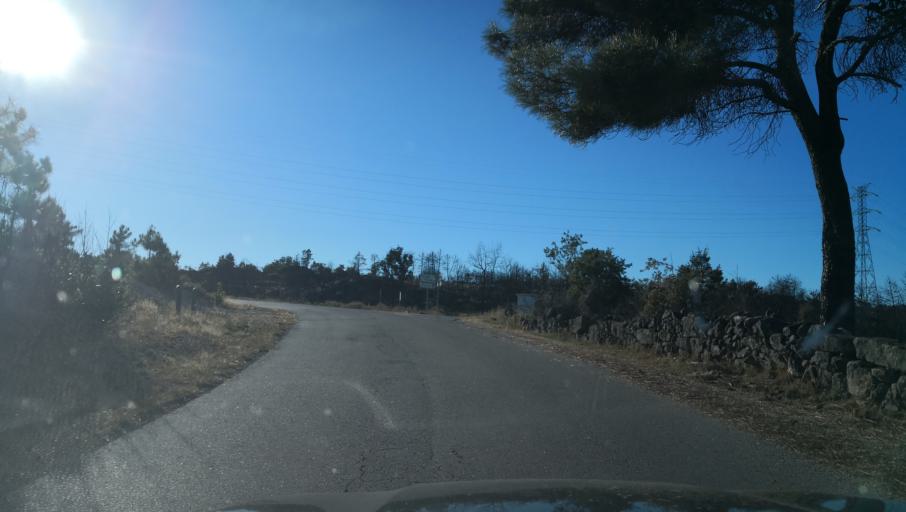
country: PT
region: Vila Real
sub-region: Sabrosa
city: Sabrosa
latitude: 41.3273
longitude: -7.6162
